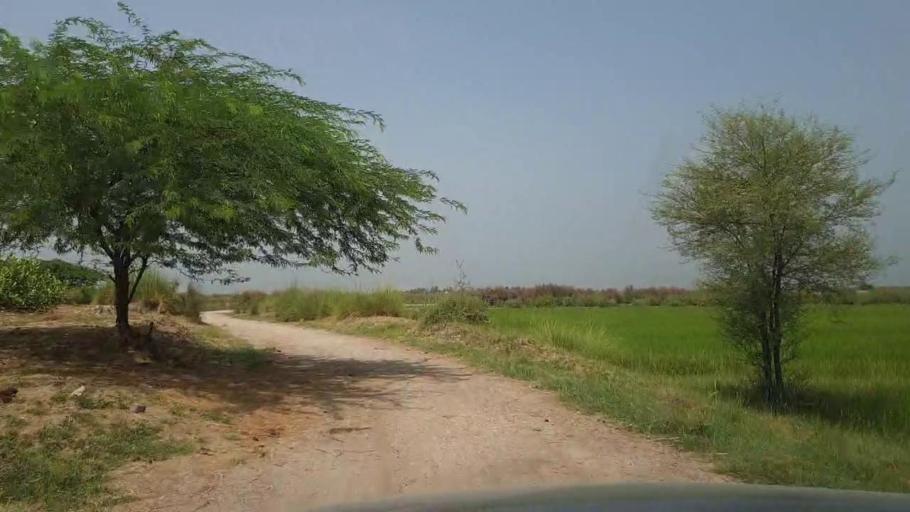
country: PK
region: Sindh
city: Madeji
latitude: 27.8135
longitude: 68.5099
